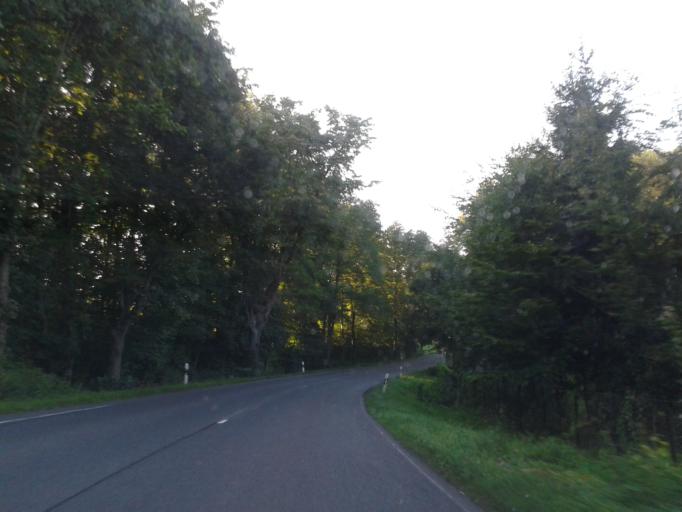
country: DE
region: Saxony
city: Wilsdruff
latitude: 51.0630
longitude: 13.5213
